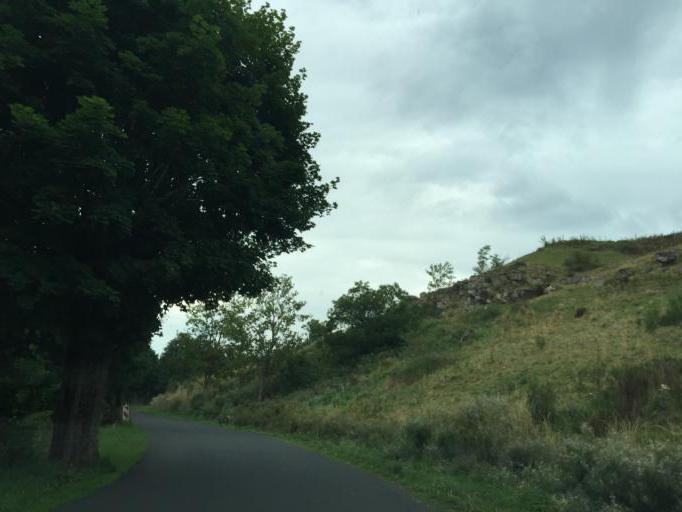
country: FR
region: Languedoc-Roussillon
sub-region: Departement de la Lozere
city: Langogne
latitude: 44.8360
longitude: 3.8083
